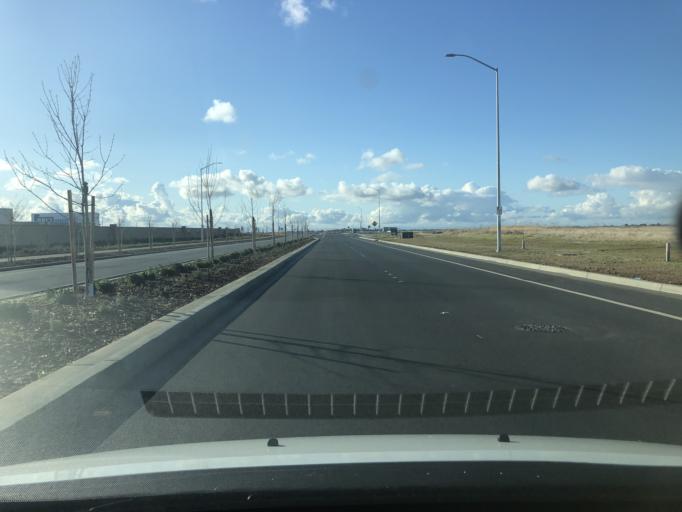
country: US
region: California
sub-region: Sacramento County
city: North Highlands
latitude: 38.7754
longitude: -121.3938
